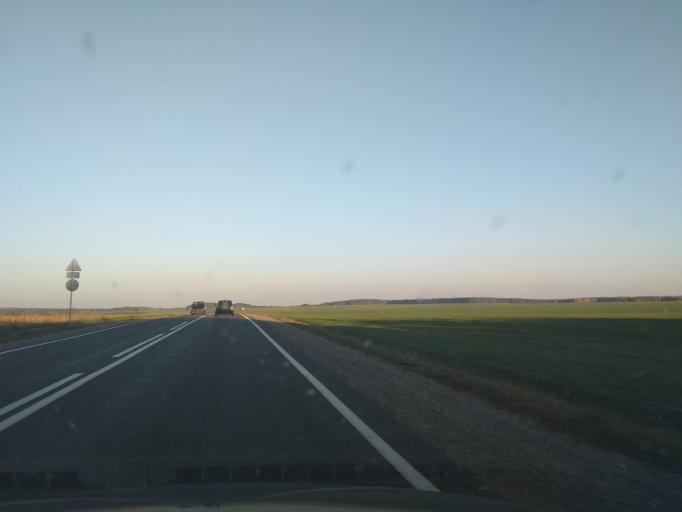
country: BY
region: Grodnenskaya
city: Zel'va
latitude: 53.1410
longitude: 24.6734
